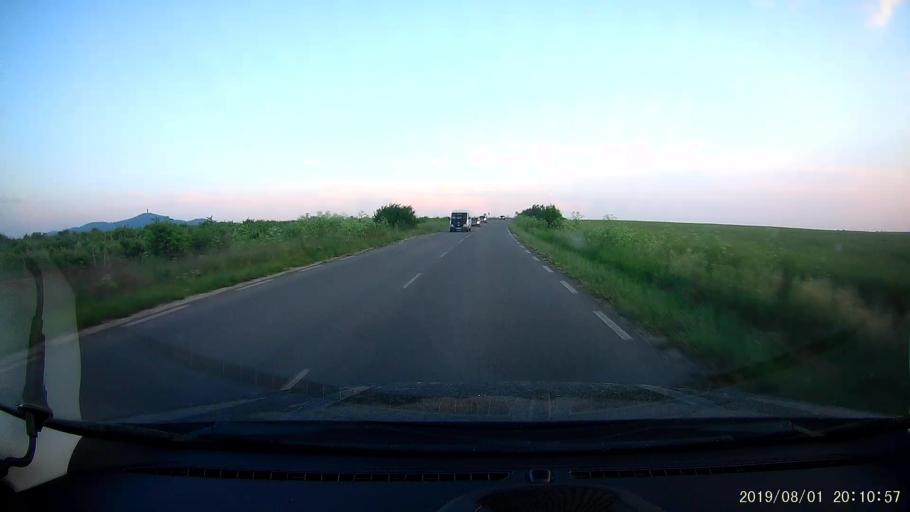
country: BG
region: Yambol
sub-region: Obshtina Yambol
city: Yambol
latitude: 42.4711
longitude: 26.6043
